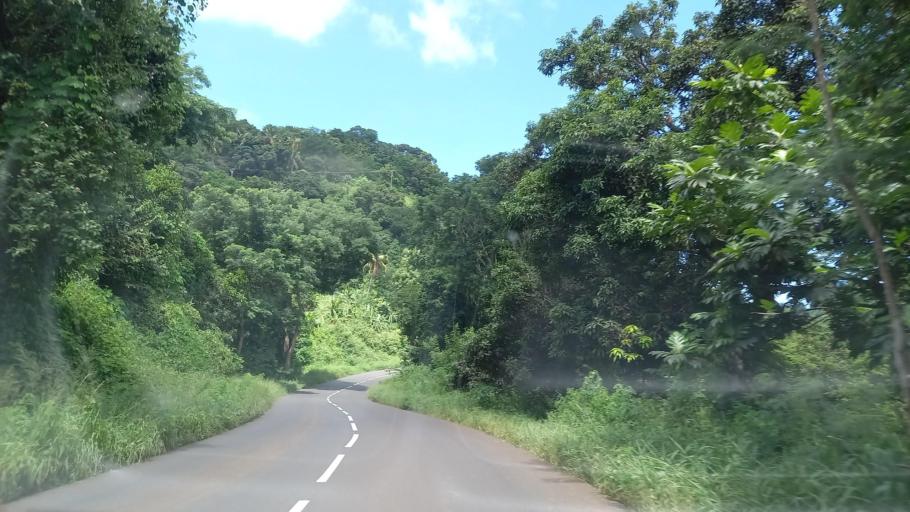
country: YT
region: Acoua
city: Acoua
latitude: -12.7327
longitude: 45.0570
